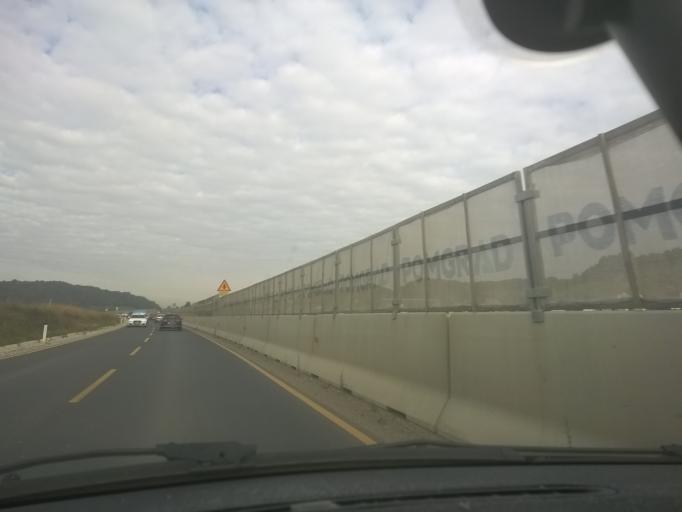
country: SI
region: Podlehnik
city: Podlehnik
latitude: 46.3409
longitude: 15.8749
